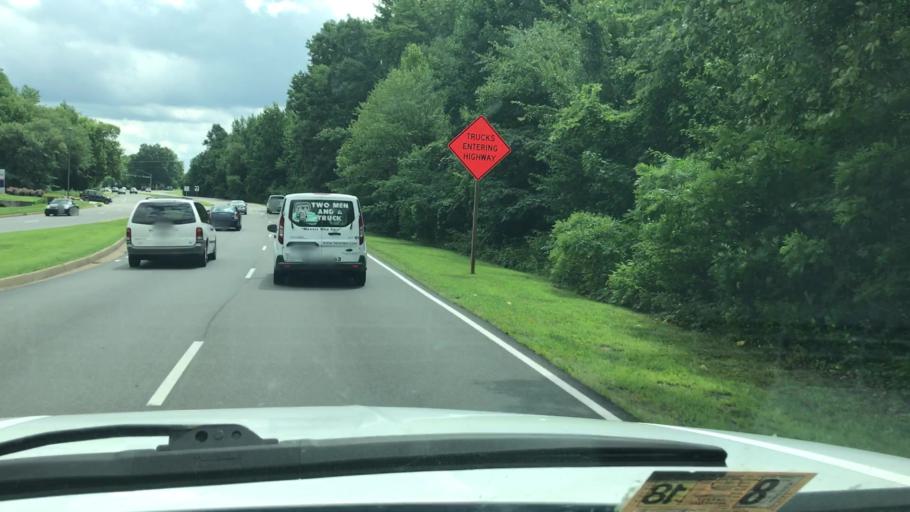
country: US
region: Virginia
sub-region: Henrico County
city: Laurel
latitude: 37.6297
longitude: -77.5239
